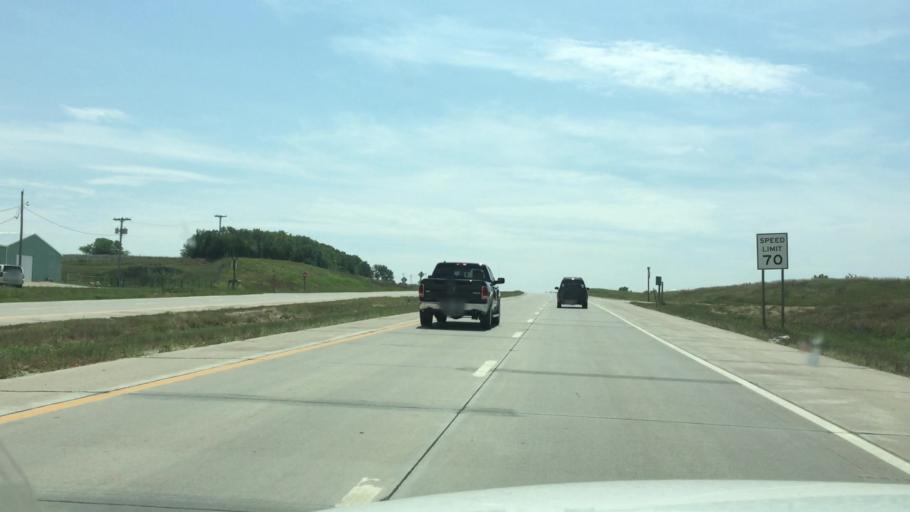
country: US
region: Kansas
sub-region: Jackson County
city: Holton
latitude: 39.4512
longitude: -95.7482
